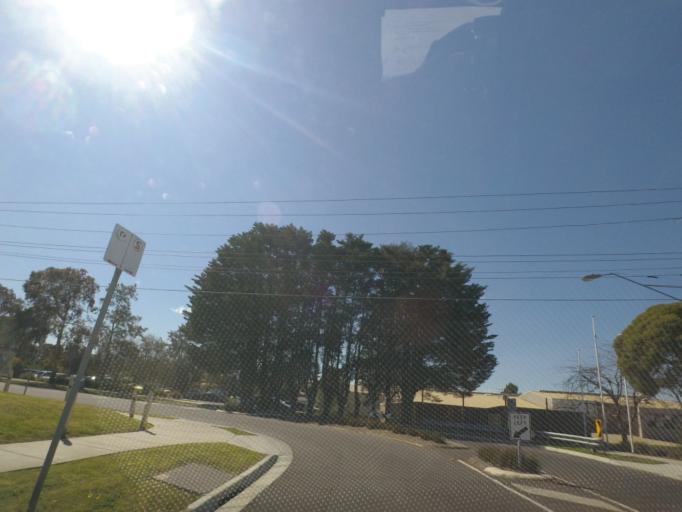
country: AU
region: Victoria
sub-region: Knox
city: Wantirna
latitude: -37.8570
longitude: 145.2288
